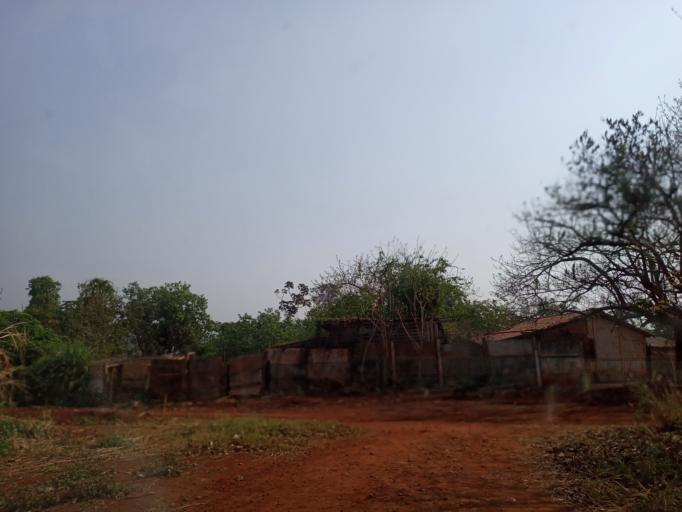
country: BR
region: Minas Gerais
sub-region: Ituiutaba
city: Ituiutaba
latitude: -18.9613
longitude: -49.4757
